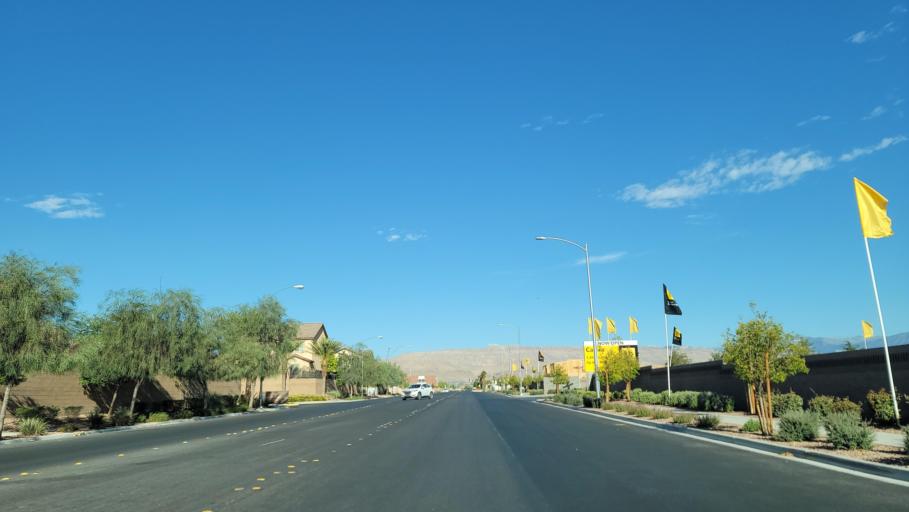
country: US
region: Nevada
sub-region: Clark County
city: Spring Valley
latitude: 36.0777
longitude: -115.2681
